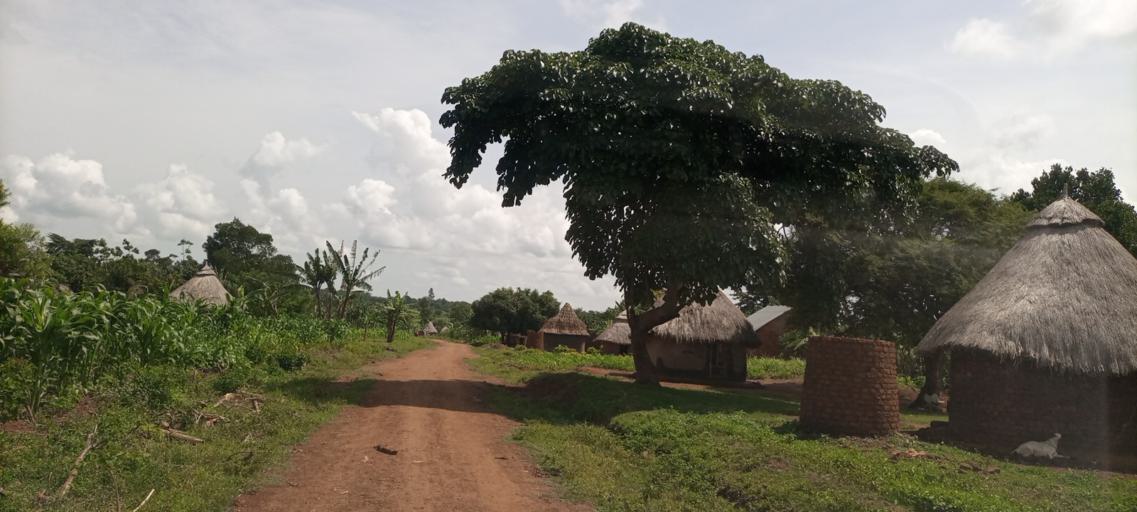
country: UG
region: Eastern Region
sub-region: Budaka District
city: Budaka
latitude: 1.1723
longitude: 33.9567
